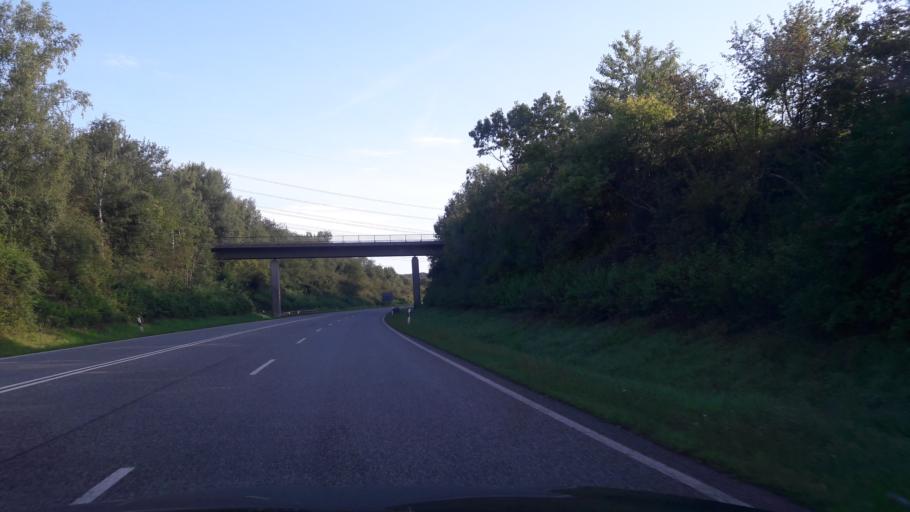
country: DE
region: Saarland
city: Heusweiler
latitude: 49.3664
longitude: 6.9245
